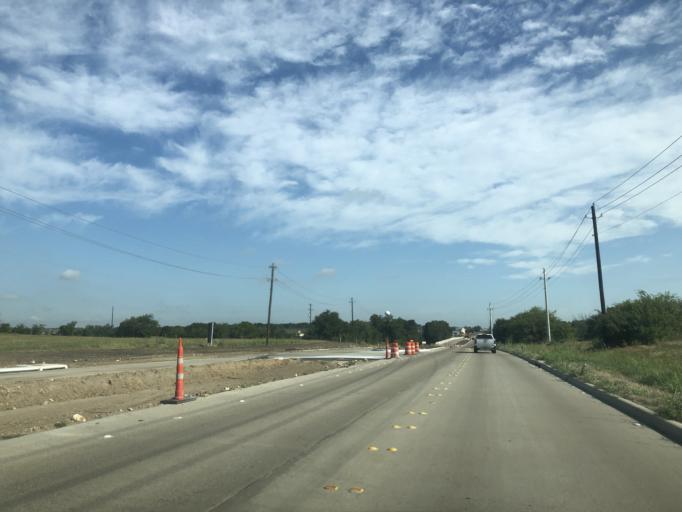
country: US
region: Texas
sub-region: Denton County
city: Justin
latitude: 33.0728
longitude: -97.2955
